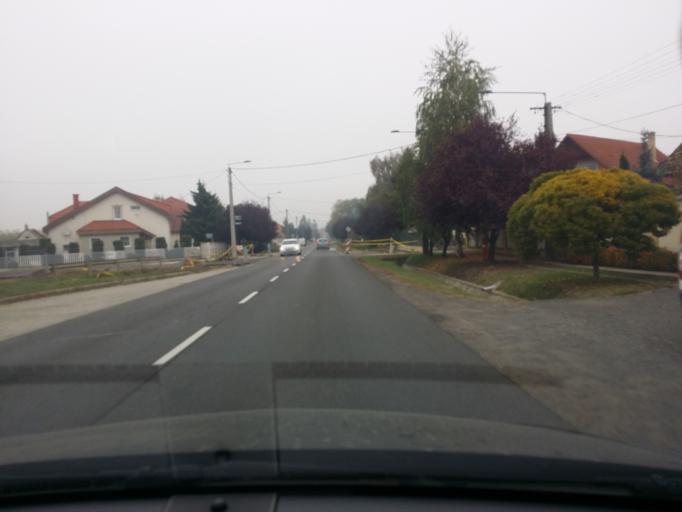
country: HU
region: Szabolcs-Szatmar-Bereg
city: Nyirpazony
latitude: 48.0098
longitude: 21.8271
